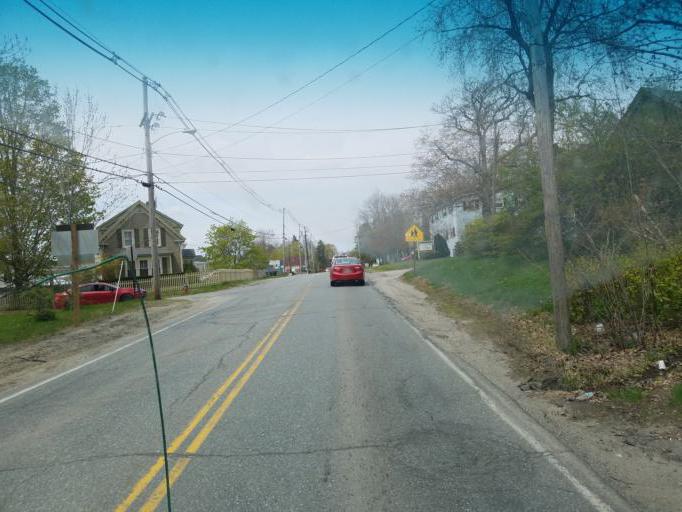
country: US
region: Maine
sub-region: Hancock County
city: Ellsworth
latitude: 44.5465
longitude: -68.4228
